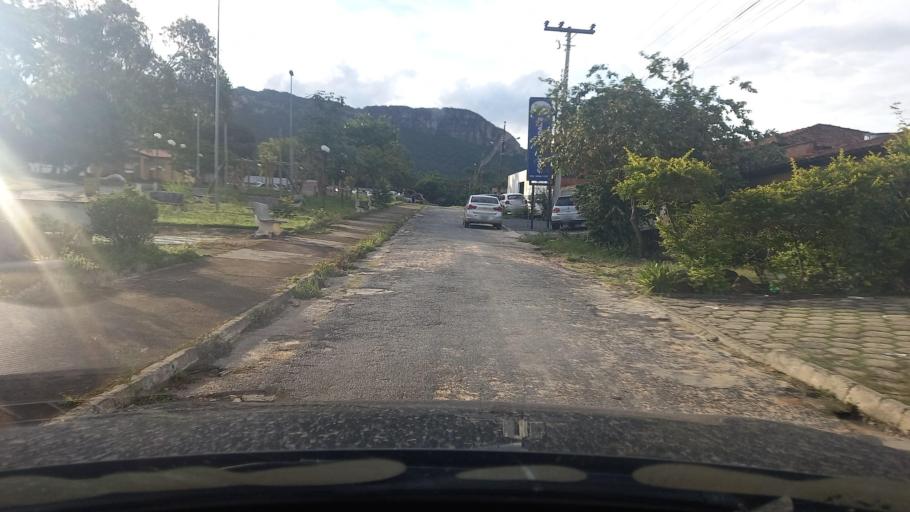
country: BR
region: Goias
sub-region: Cavalcante
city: Cavalcante
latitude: -13.7971
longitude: -47.4616
